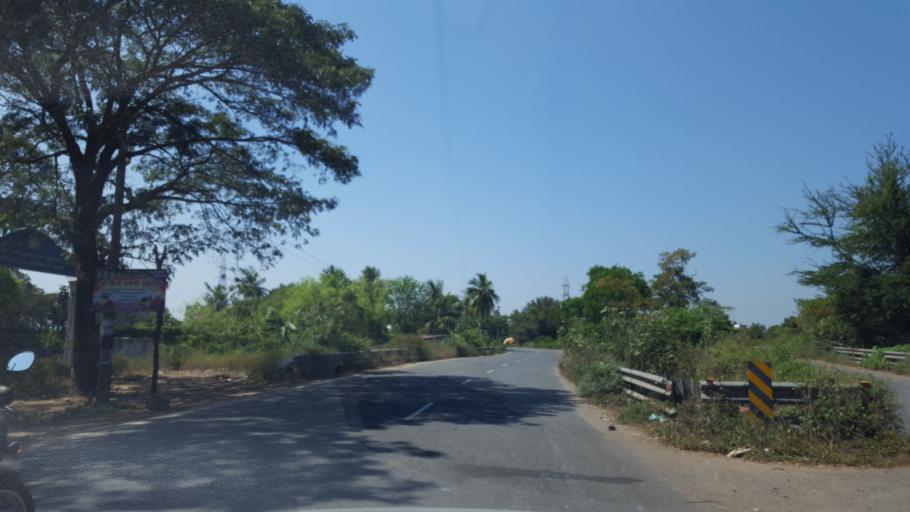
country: IN
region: Tamil Nadu
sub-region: Kancheepuram
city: Chengalpattu
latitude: 12.7544
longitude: 79.9284
